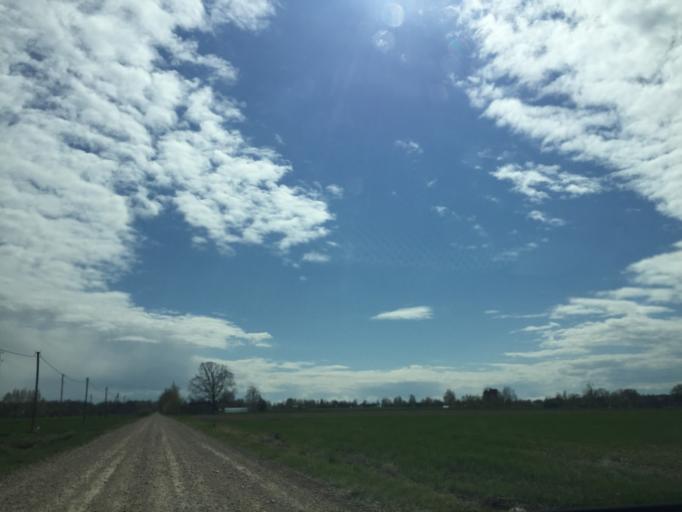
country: LV
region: Jelgava
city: Jelgava
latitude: 56.5691
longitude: 23.7826
